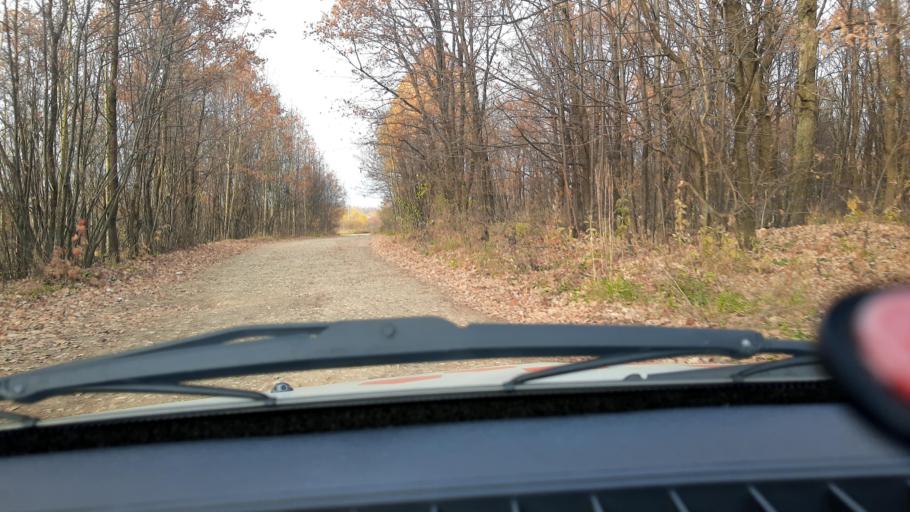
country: RU
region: Bashkortostan
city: Iglino
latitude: 54.7948
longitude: 56.3347
